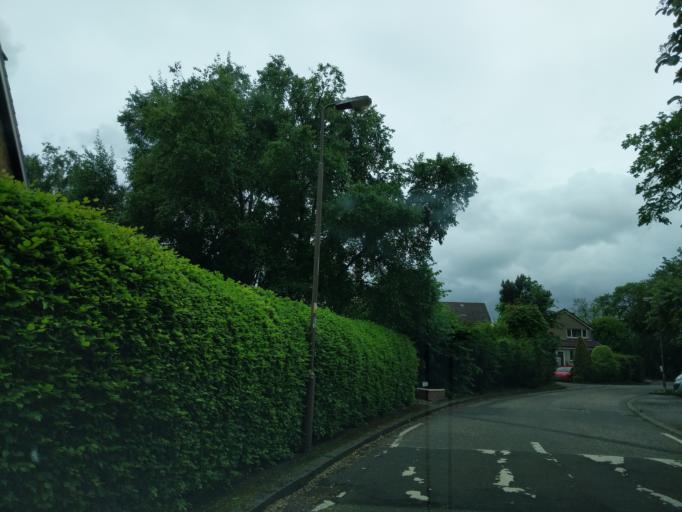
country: GB
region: Scotland
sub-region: Edinburgh
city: Colinton
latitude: 55.9488
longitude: -3.2836
